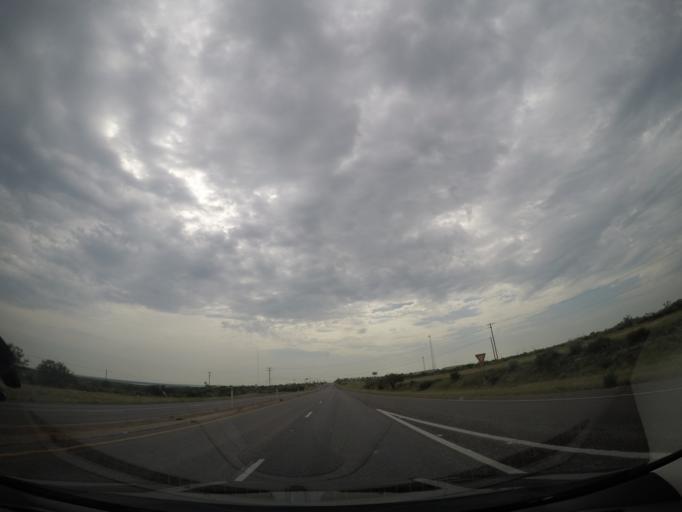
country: US
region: Texas
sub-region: Val Verde County
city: Cienegas Terrace
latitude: 29.4670
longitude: -101.0165
